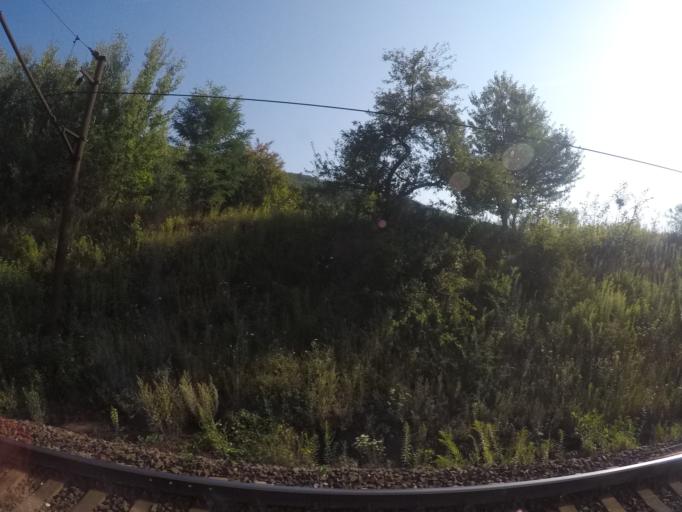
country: SK
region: Presovsky
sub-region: Okres Presov
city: Presov
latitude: 48.8608
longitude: 21.2203
